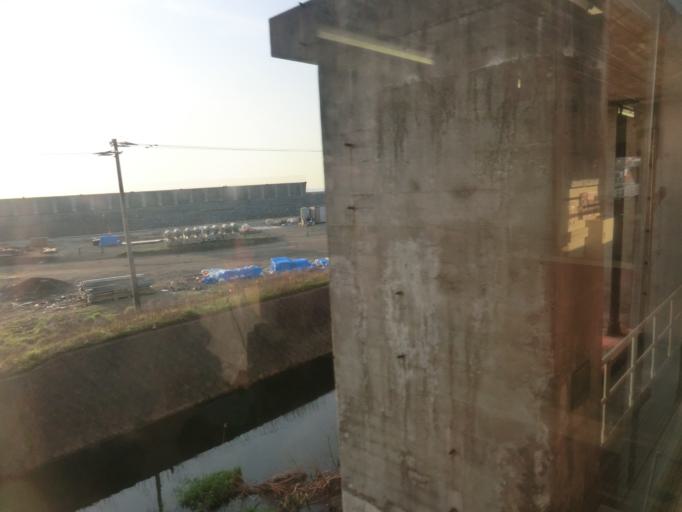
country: JP
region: Iwate
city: Miyako
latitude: 40.1074
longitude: 141.8249
